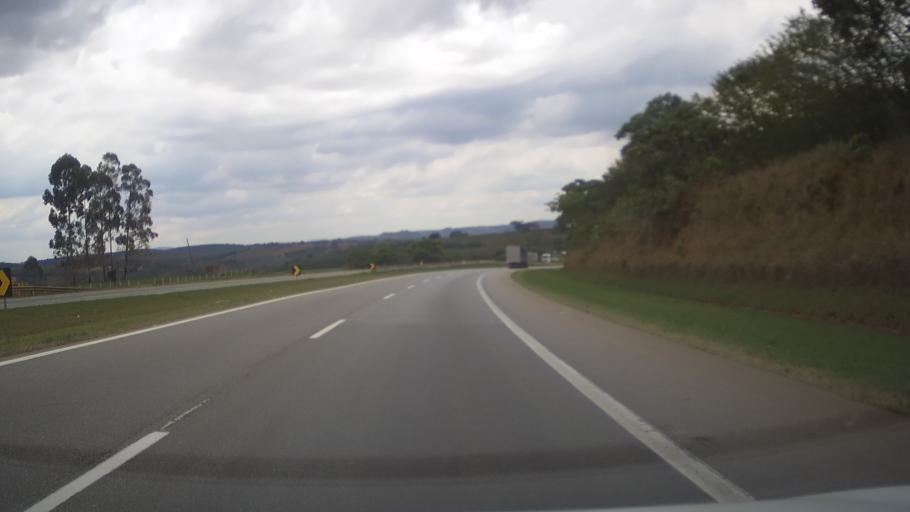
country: BR
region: Minas Gerais
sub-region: Nepomuceno
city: Nepomuceno
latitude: -21.4671
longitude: -45.2060
